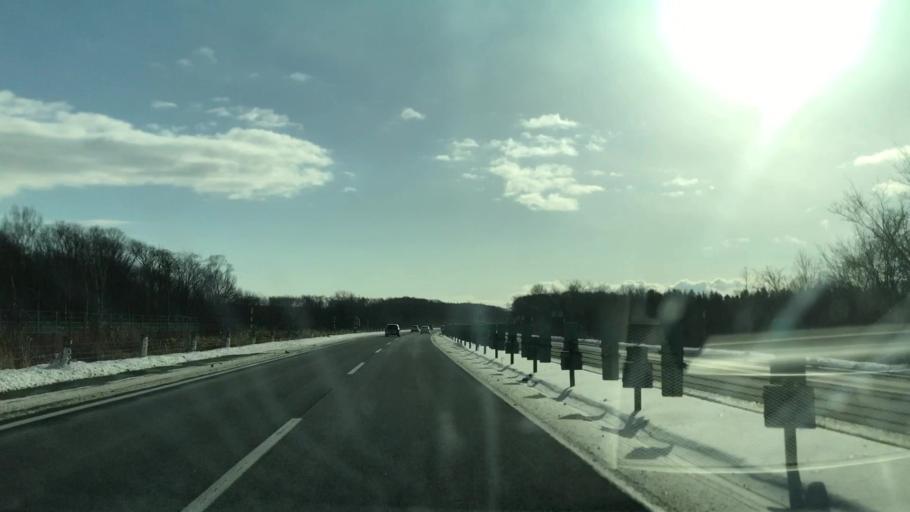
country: JP
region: Hokkaido
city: Chitose
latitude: 42.8373
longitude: 141.6047
